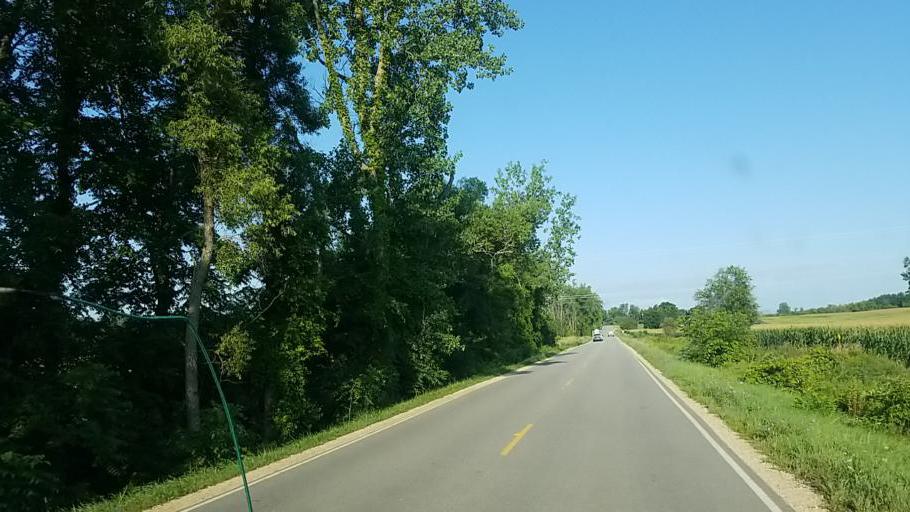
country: US
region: Michigan
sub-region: Newaygo County
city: Newaygo
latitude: 43.3511
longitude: -85.8275
